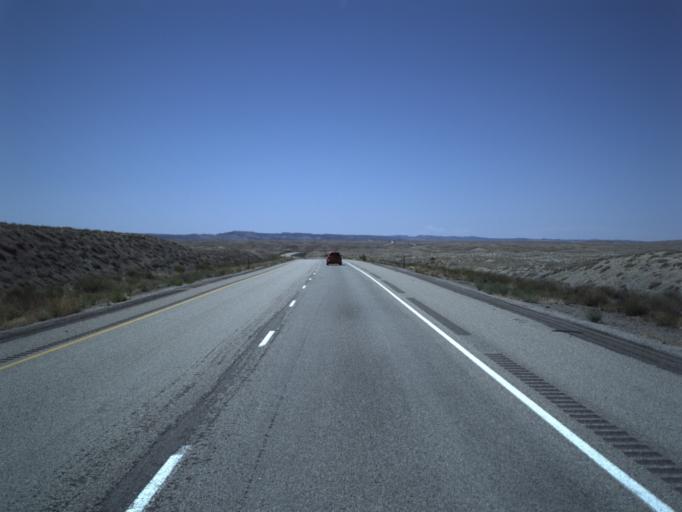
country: US
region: Utah
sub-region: Grand County
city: Moab
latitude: 38.9926
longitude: -109.3325
